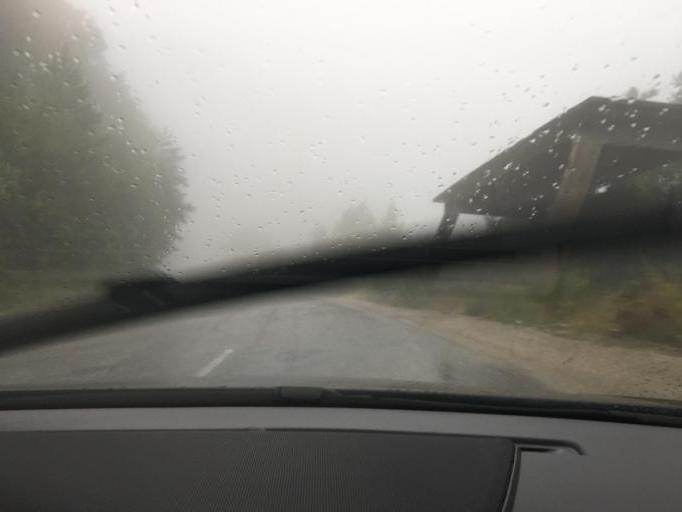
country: MK
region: Kriva Palanka
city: Kriva Palanka
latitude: 42.2190
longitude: 22.4654
